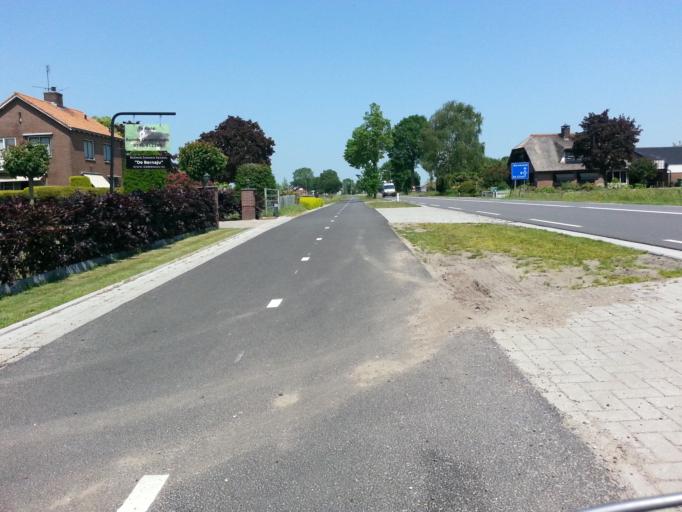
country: NL
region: Gelderland
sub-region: Gemeente Barneveld
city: Barneveld
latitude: 52.1171
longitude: 5.5393
